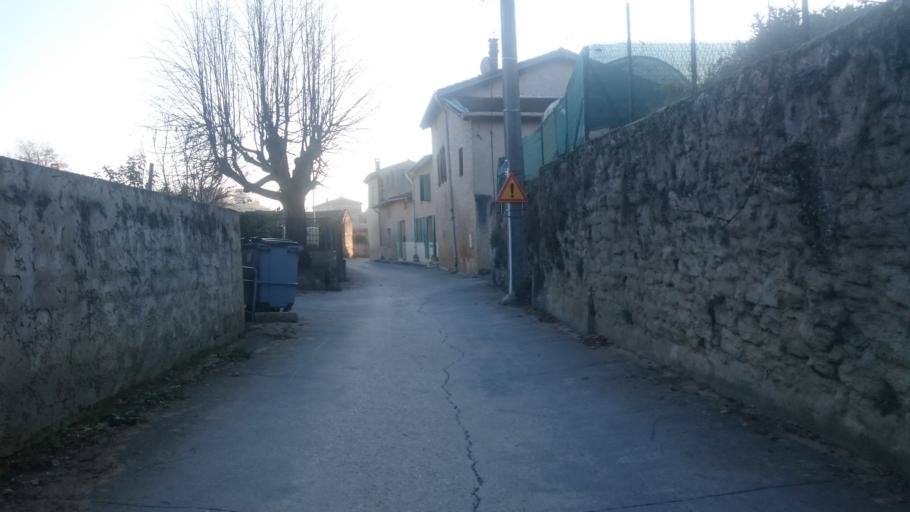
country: FR
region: Rhone-Alpes
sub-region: Departement de la Drome
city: Clerieux
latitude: 45.0780
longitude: 4.9596
